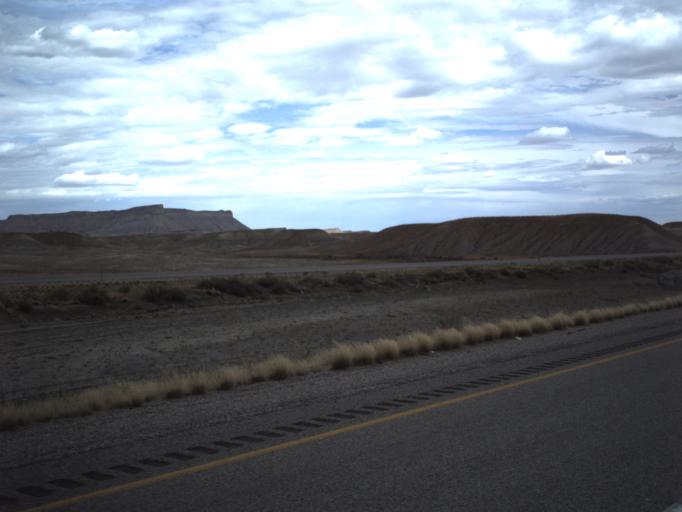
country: US
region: Utah
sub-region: Grand County
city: Moab
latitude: 38.9453
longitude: -110.0400
